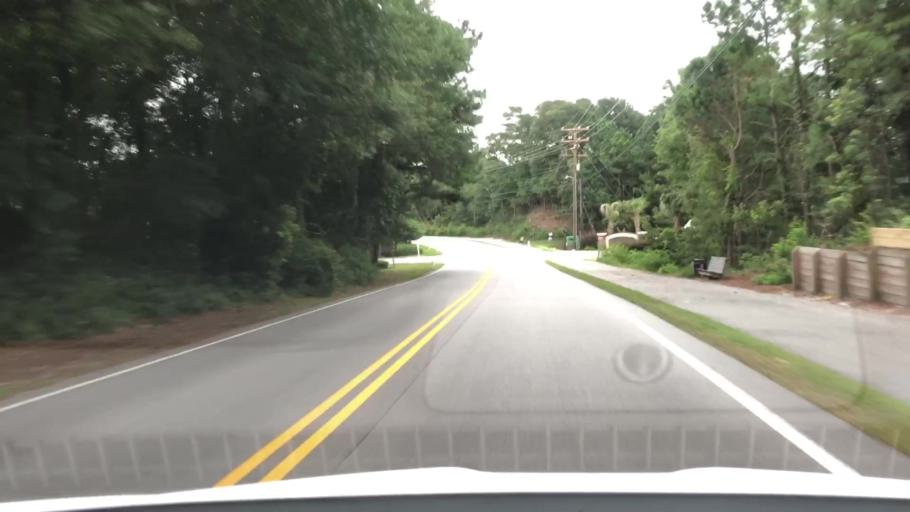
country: US
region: North Carolina
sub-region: Carteret County
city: Cedar Point
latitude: 34.6576
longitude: -77.0750
